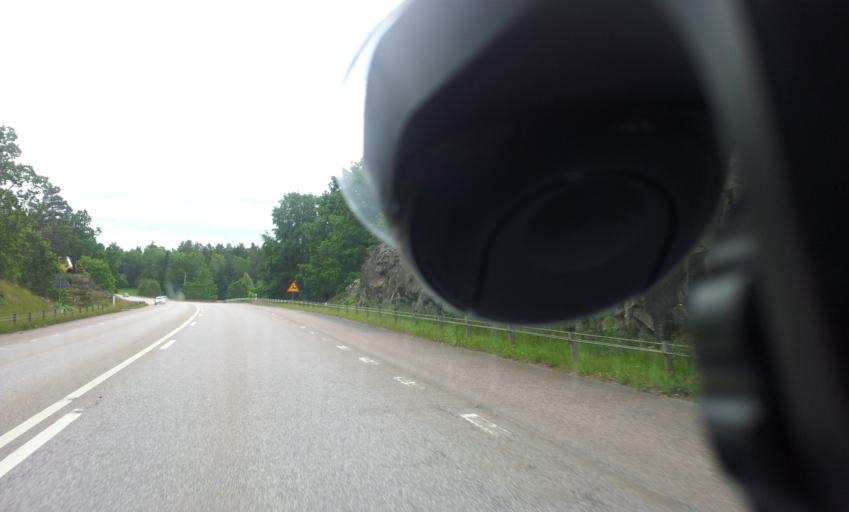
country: SE
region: Kalmar
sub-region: Vasterviks Kommun
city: Ankarsrum
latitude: 57.6685
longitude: 16.4415
